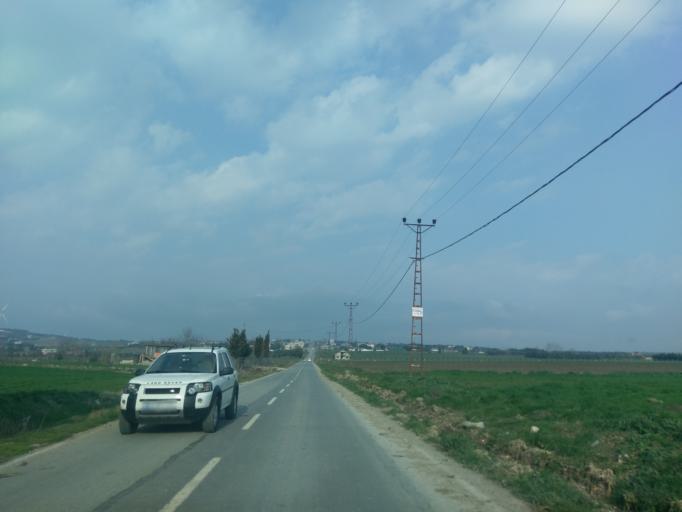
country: TR
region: Istanbul
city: Kavakli
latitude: 41.1191
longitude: 28.3114
